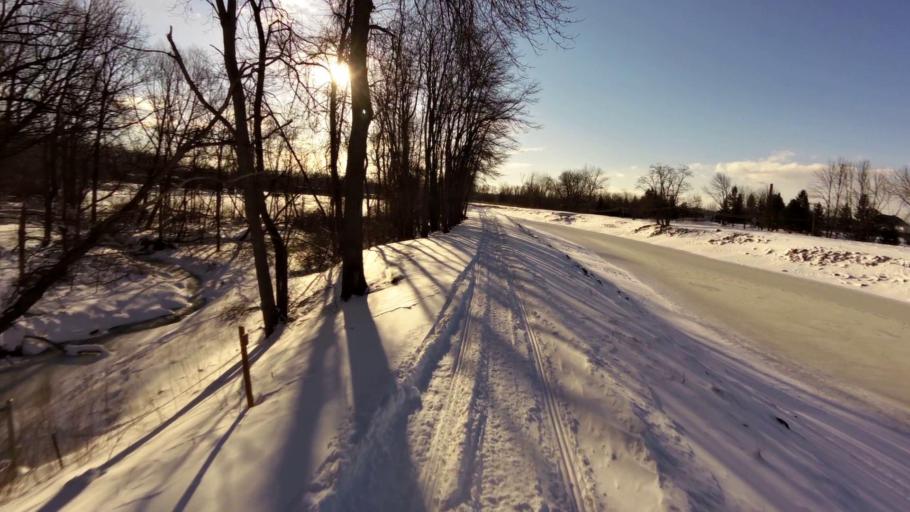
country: US
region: New York
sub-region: Orleans County
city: Albion
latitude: 43.2491
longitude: -78.2135
